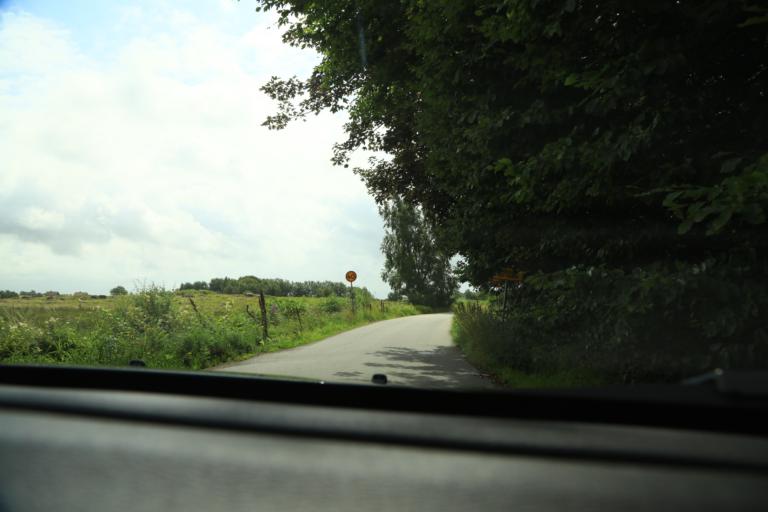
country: SE
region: Halland
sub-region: Varbergs Kommun
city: Traslovslage
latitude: 57.1154
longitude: 12.3091
